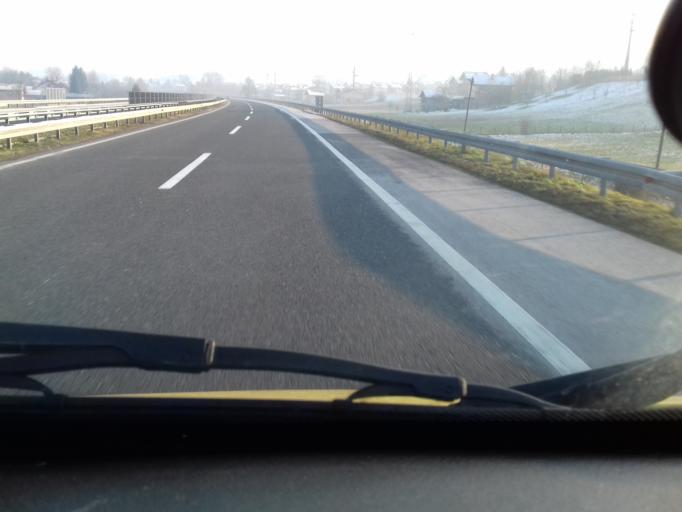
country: BA
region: Federation of Bosnia and Herzegovina
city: Gornje Mostre
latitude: 44.0141
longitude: 18.1390
